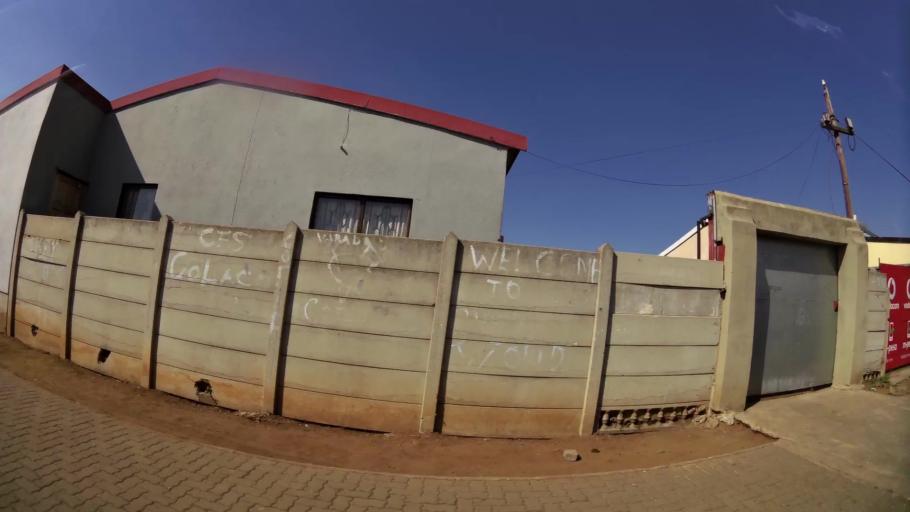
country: ZA
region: Gauteng
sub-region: City of Johannesburg Metropolitan Municipality
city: Johannesburg
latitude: -26.1837
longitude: 27.9775
